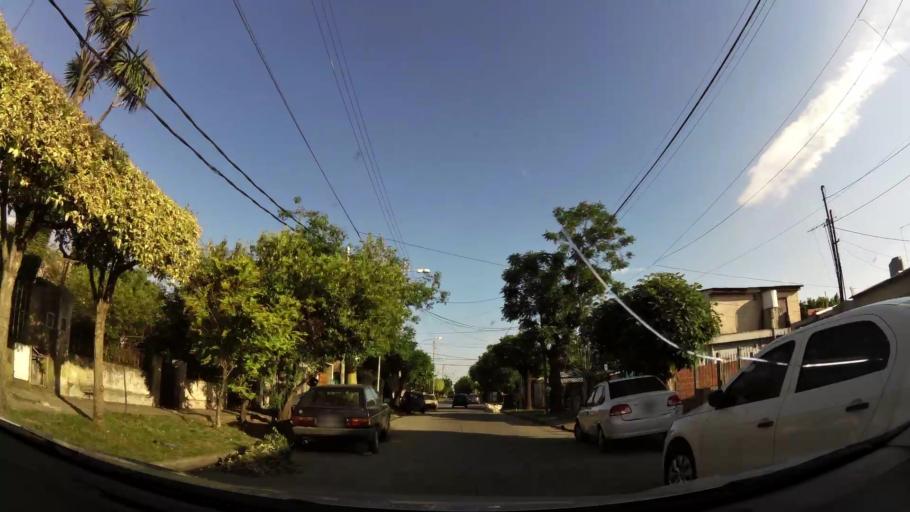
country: AR
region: Buenos Aires
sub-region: Partido de Tigre
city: Tigre
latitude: -34.4658
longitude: -58.6633
